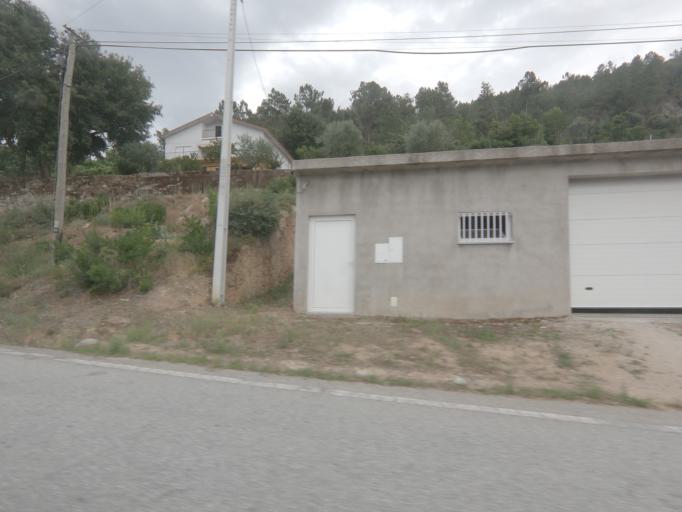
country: PT
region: Viseu
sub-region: Armamar
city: Armamar
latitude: 41.1196
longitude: -7.6679
